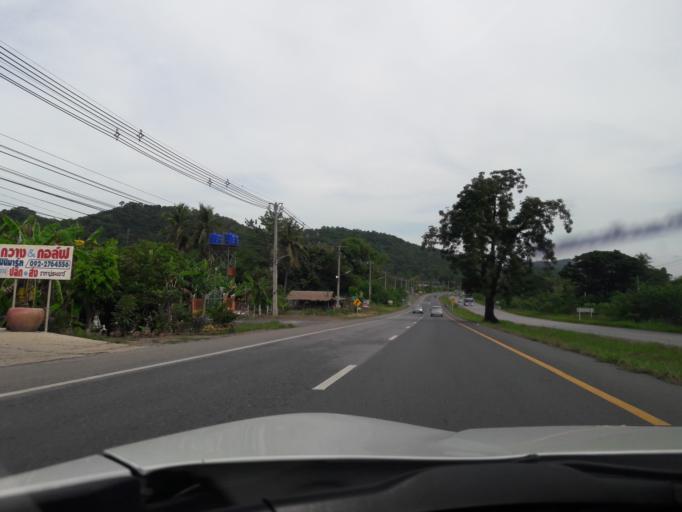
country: TH
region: Lop Buri
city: Chai Badan
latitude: 15.2755
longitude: 101.1241
